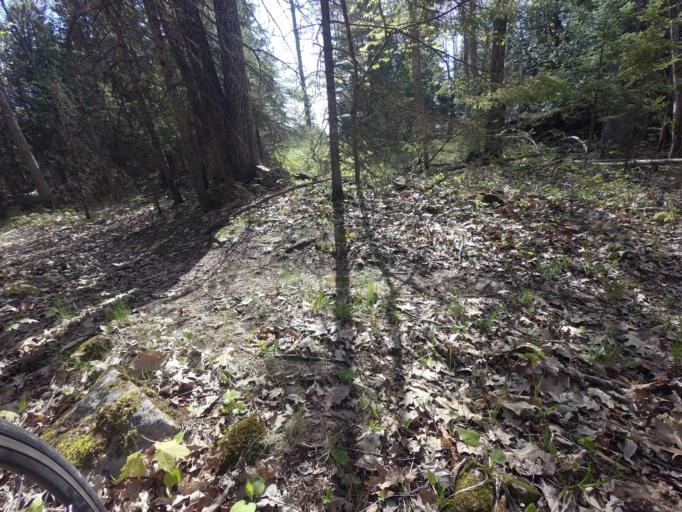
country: CA
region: Ontario
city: Arnprior
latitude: 45.4684
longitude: -76.3004
